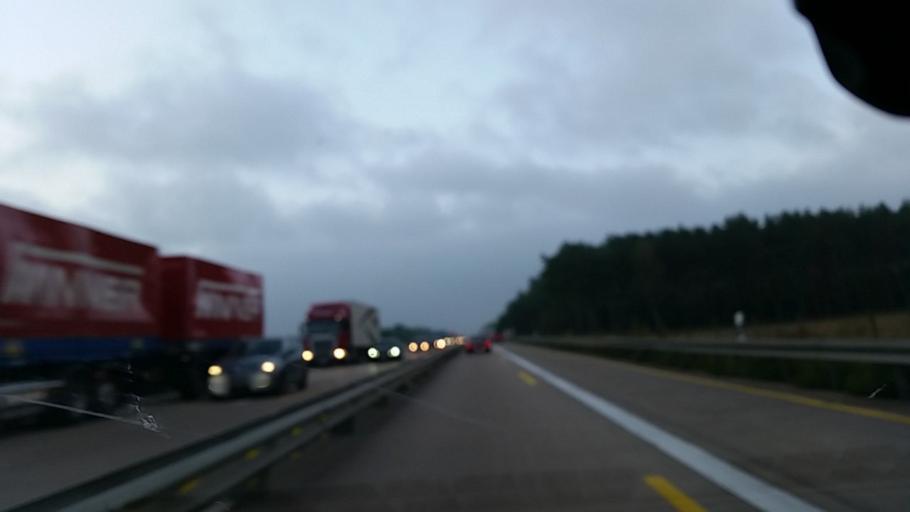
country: DE
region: Lower Saxony
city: Lindwedel
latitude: 52.6437
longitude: 9.7109
